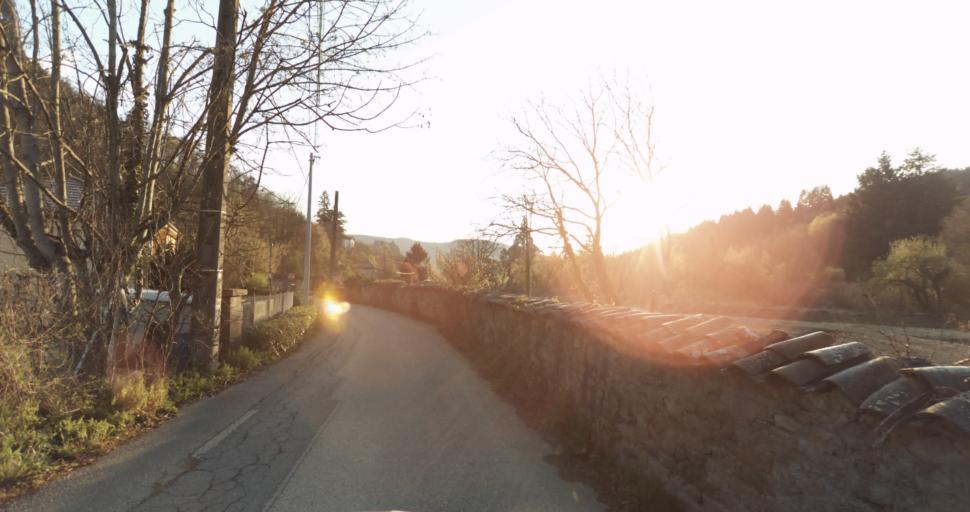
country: FR
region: Rhone-Alpes
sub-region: Departement du Rhone
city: Tarare
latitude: 45.8936
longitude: 4.4162
